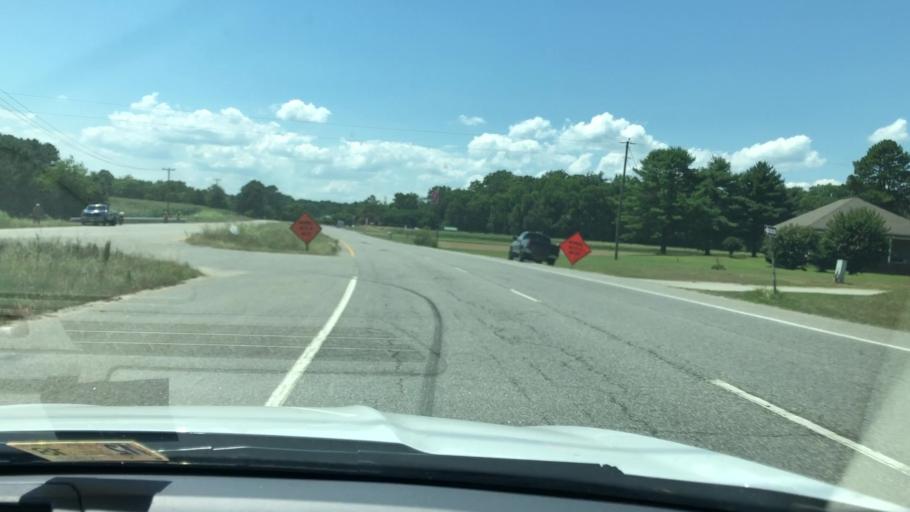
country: US
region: Virginia
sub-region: Middlesex County
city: Saluda
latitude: 37.6035
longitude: -76.5270
